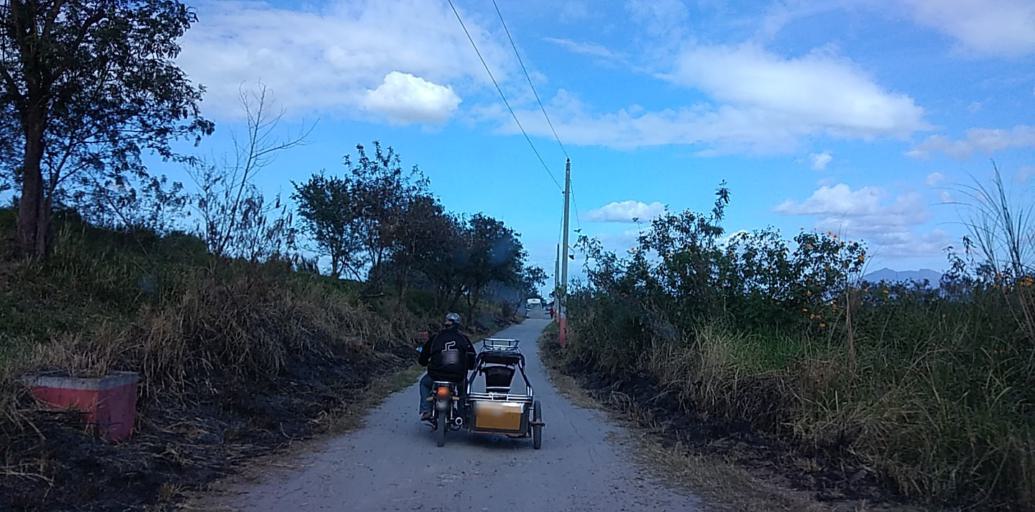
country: PH
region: Central Luzon
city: Santol
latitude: 15.1443
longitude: 120.5294
